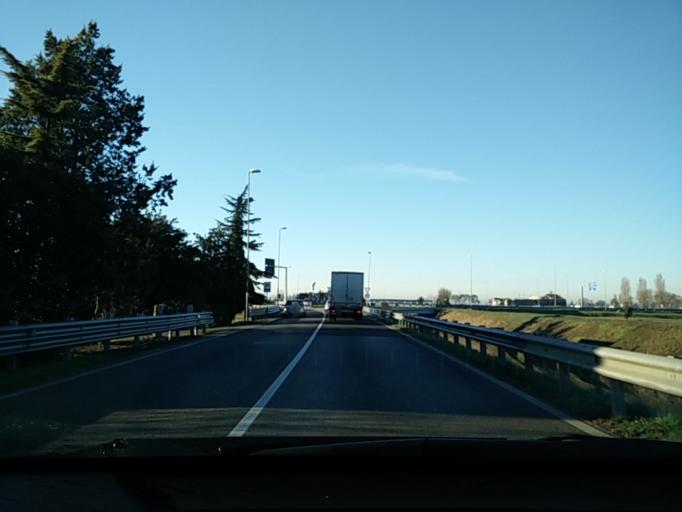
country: IT
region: Veneto
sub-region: Provincia di Venezia
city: Fossalta di Piave
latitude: 45.6148
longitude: 12.4927
